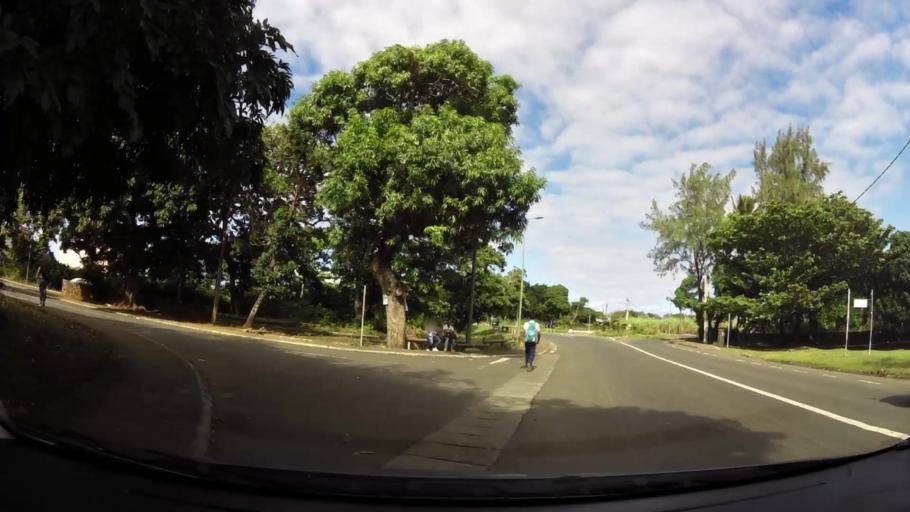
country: MU
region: Grand Port
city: Beau Vallon
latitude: -20.4219
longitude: 57.7022
